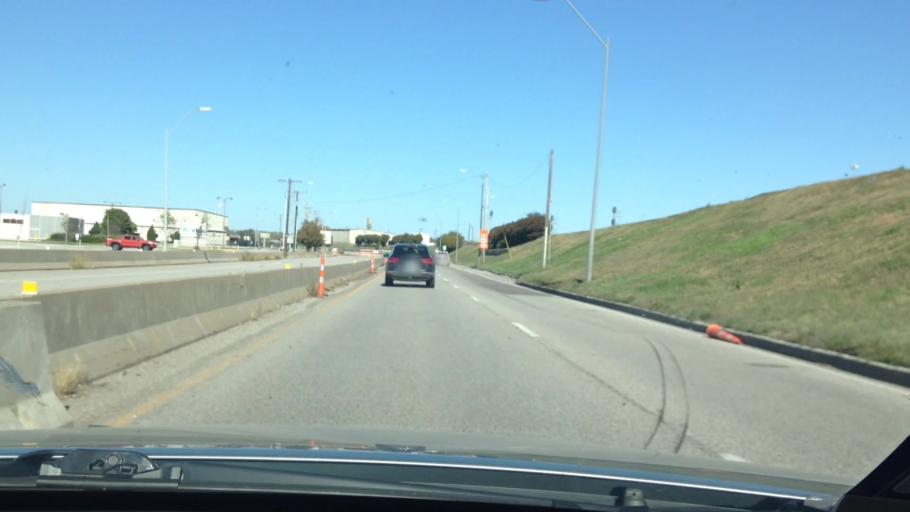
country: US
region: Missouri
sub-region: Jackson County
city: Kansas City
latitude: 39.1196
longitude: -94.5892
